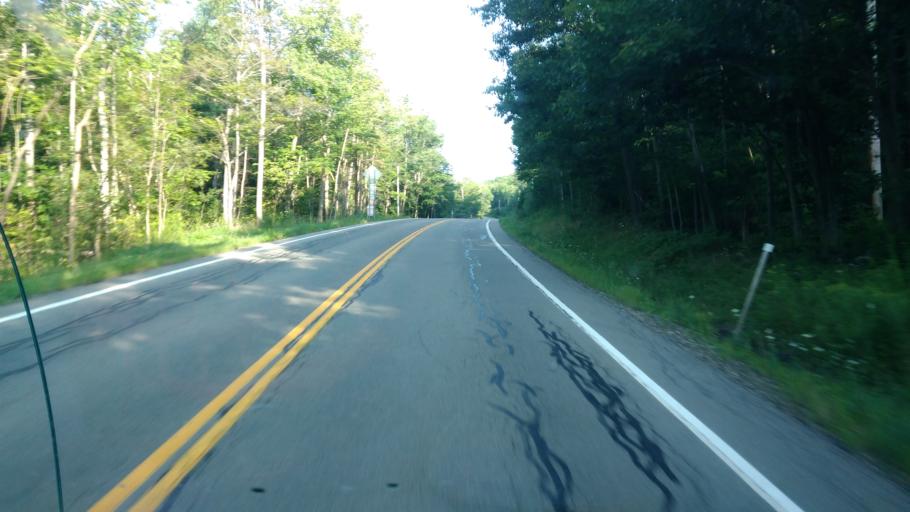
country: US
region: New York
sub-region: Allegany County
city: Andover
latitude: 42.1492
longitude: -77.6899
